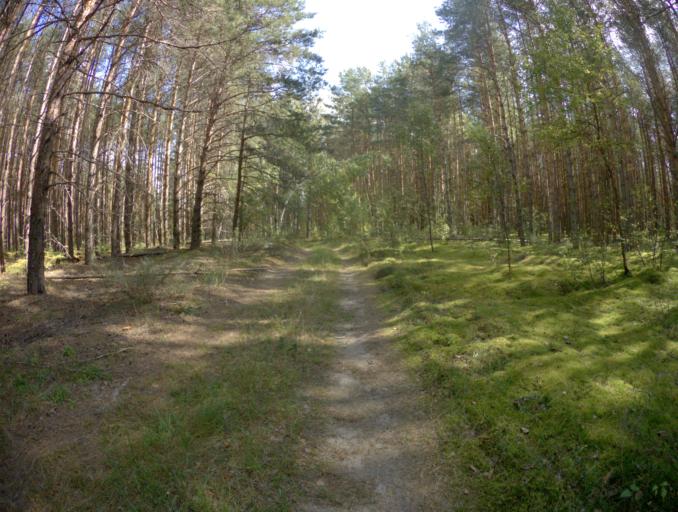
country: RU
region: Vladimir
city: Pokrov
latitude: 55.8467
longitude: 39.2509
